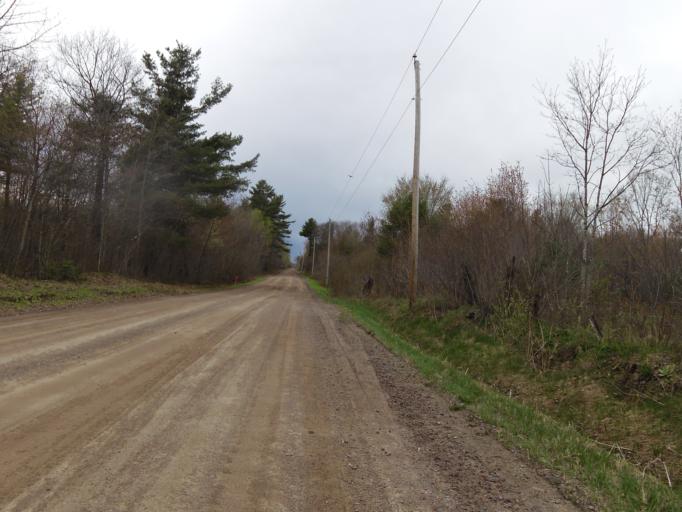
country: CA
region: Quebec
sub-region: Laurentides
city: Brownsburg-Chatham
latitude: 45.6137
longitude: -74.4917
